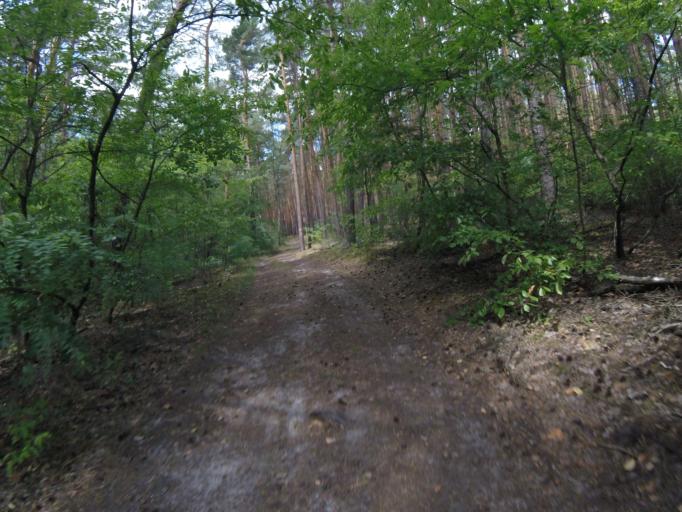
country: DE
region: Brandenburg
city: Gross Koris
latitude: 52.1984
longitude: 13.6476
